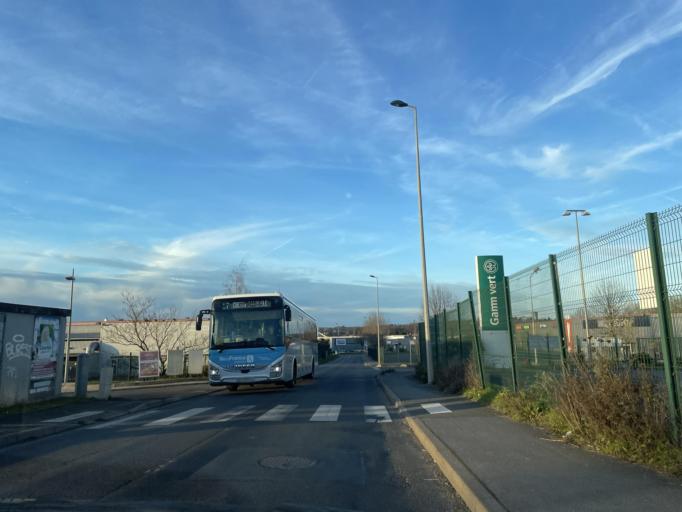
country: FR
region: Ile-de-France
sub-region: Departement de Seine-et-Marne
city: Coulommiers
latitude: 48.8029
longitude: 3.0970
